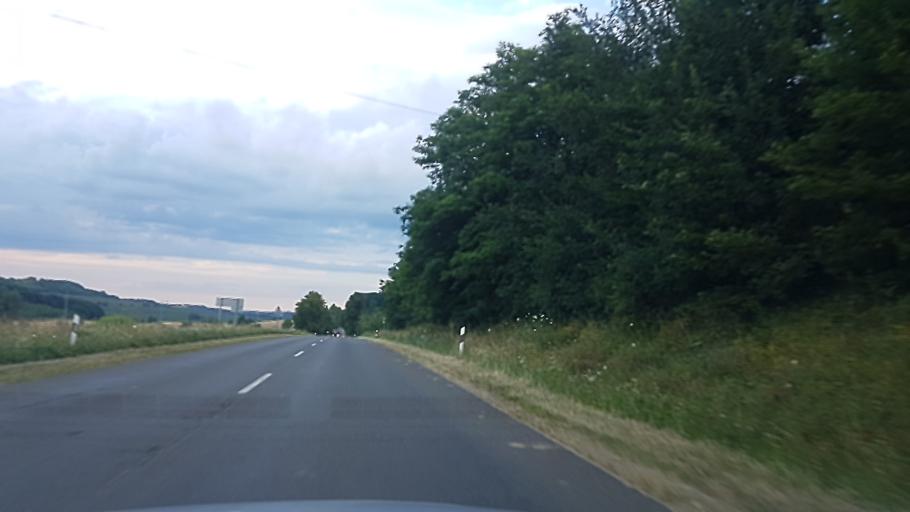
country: HU
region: Somogy
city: Kaposvar
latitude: 46.2885
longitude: 17.8184
